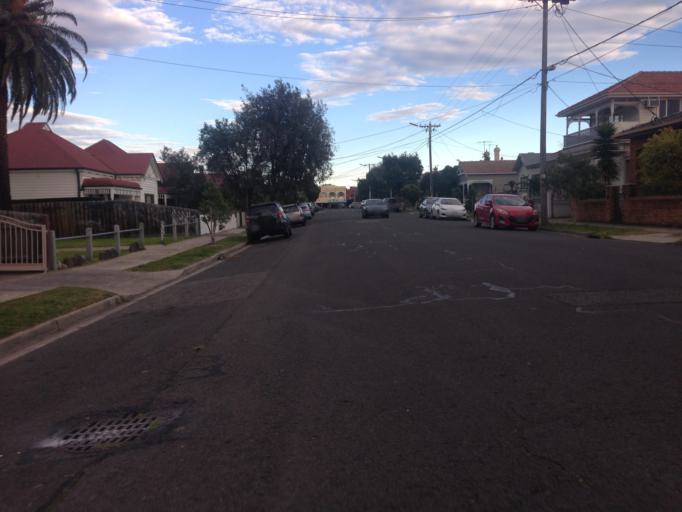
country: AU
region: Victoria
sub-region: Darebin
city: Thornbury
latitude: -37.7559
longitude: 145.0037
